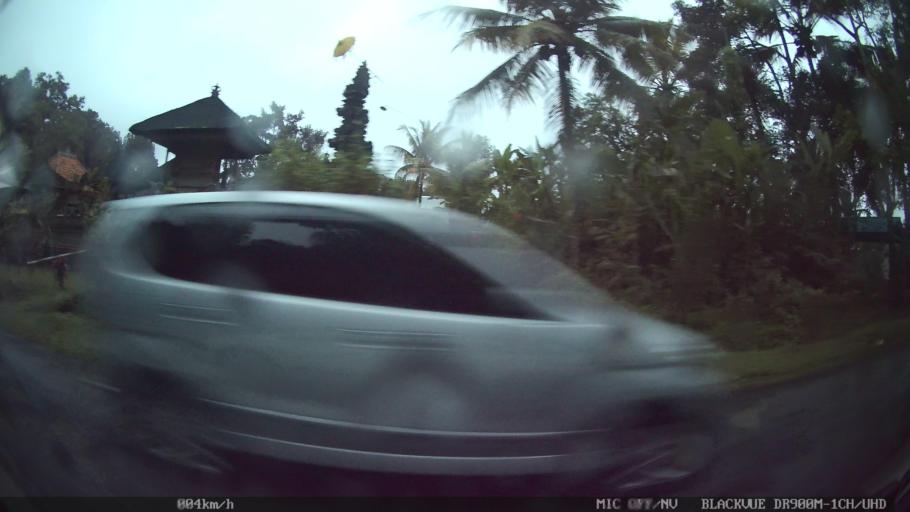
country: ID
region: Bali
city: Banjar Ponggang
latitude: -8.3817
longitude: 115.2652
